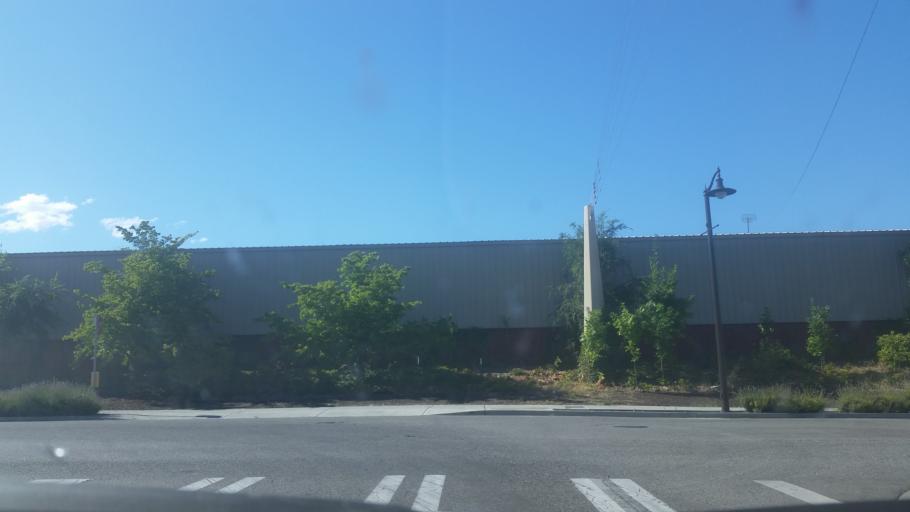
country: US
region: Washington
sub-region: Chelan County
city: Wenatchee
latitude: 47.4317
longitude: -120.3132
